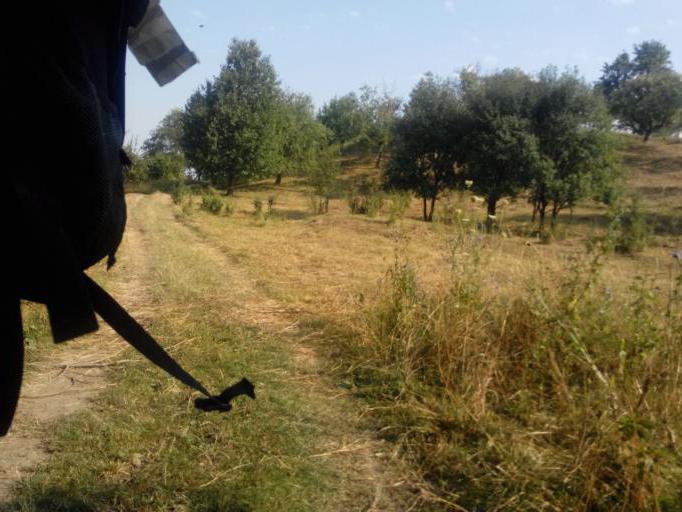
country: RO
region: Suceava
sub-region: Comuna Radaseni
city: Radaseni
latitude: 47.4625
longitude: 26.2616
